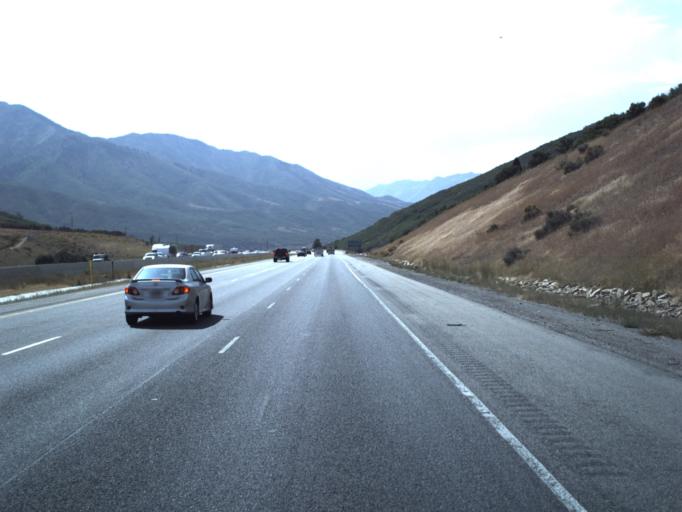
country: US
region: Utah
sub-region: Summit County
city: Summit Park
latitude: 40.7476
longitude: -111.6405
